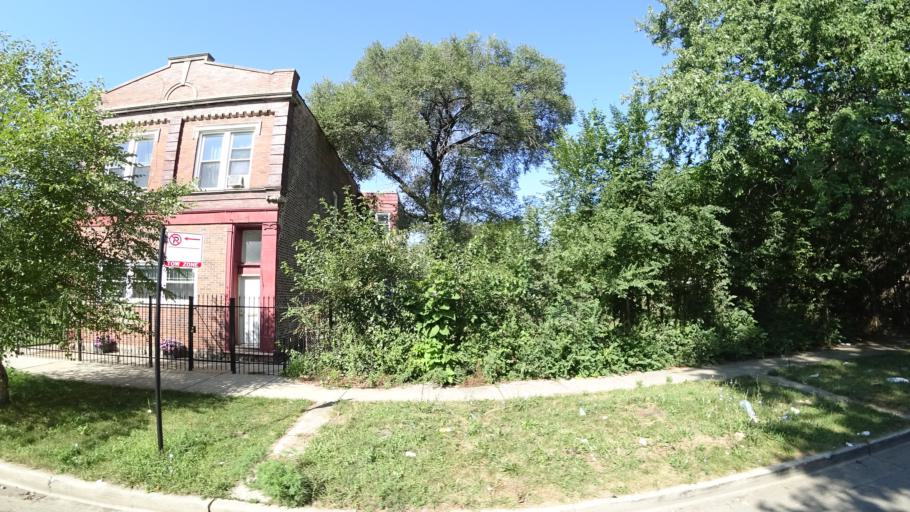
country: US
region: Illinois
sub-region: Cook County
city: Cicero
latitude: 41.8610
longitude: -87.7226
